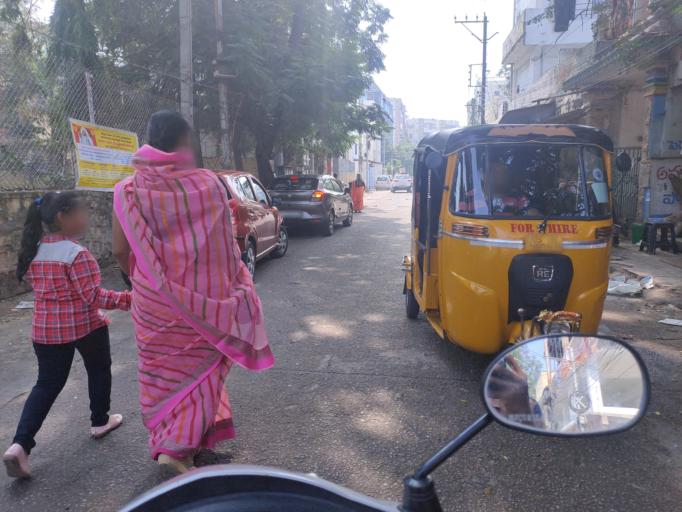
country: IN
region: Telangana
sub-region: Hyderabad
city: Malkajgiri
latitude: 17.4379
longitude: 78.4843
